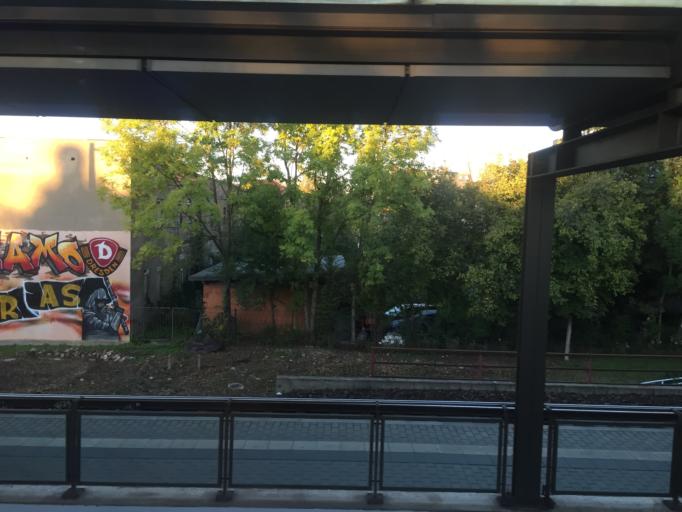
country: DE
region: Saxony
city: Heidenau
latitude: 51.0000
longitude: 13.8282
